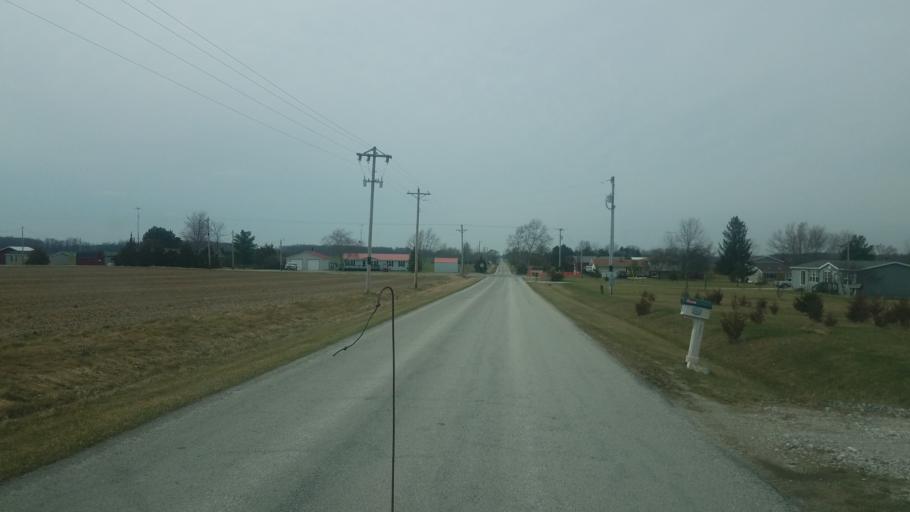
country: US
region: Ohio
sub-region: Huron County
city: Greenwich
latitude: 41.1396
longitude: -82.5365
